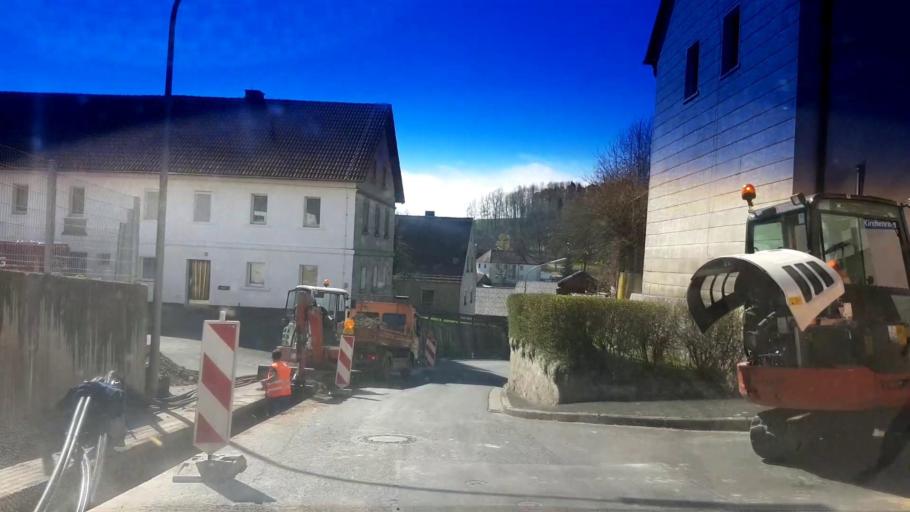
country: DE
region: Bavaria
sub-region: Upper Franconia
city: Bindlach
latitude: 50.0124
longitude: 11.6247
